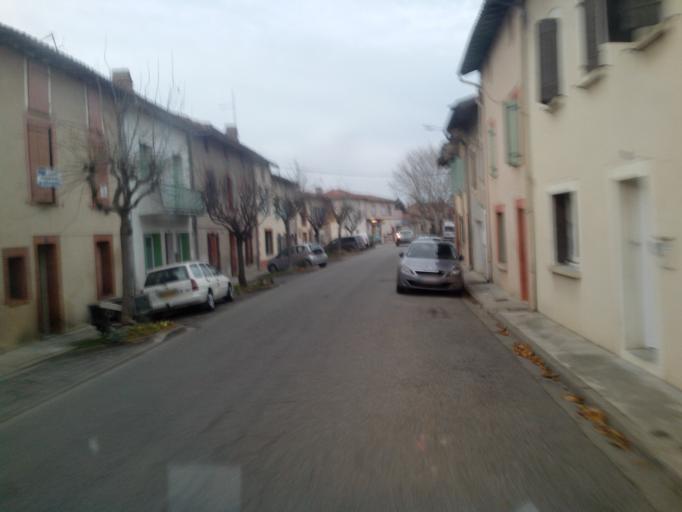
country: FR
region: Midi-Pyrenees
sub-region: Departement de l'Ariege
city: Mazeres
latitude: 43.2509
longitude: 1.6762
